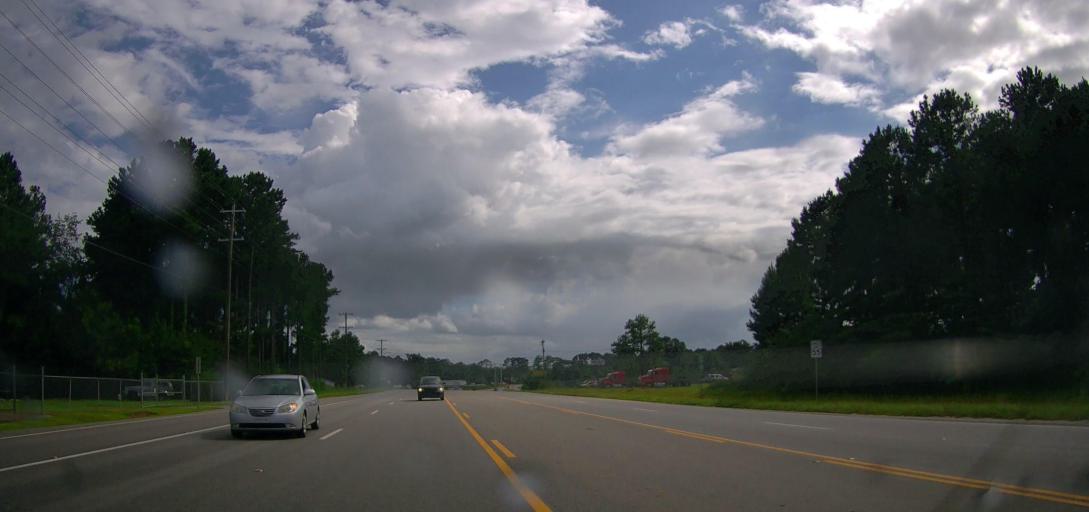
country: US
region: Georgia
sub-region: Coffee County
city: Douglas
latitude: 31.4995
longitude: -82.8280
